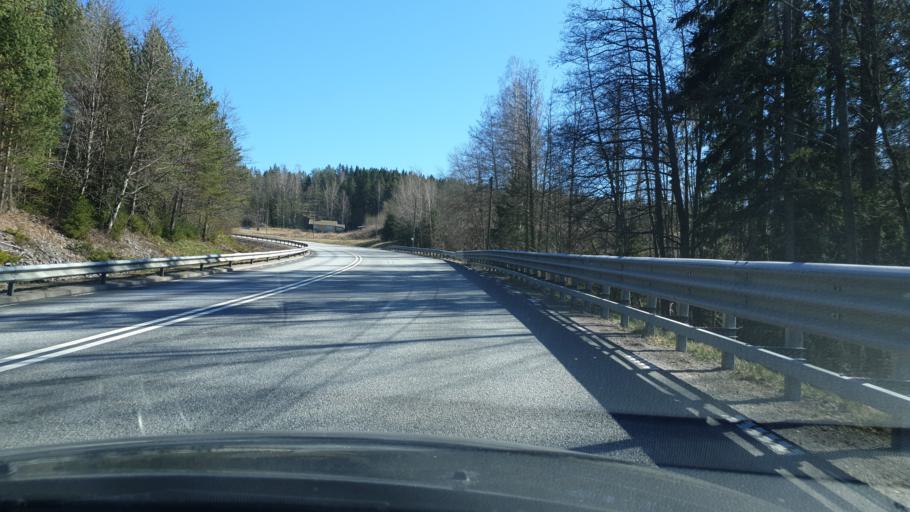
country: SE
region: Vaestra Goetaland
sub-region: Tanums Kommun
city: Tanumshede
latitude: 58.7940
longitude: 11.5758
